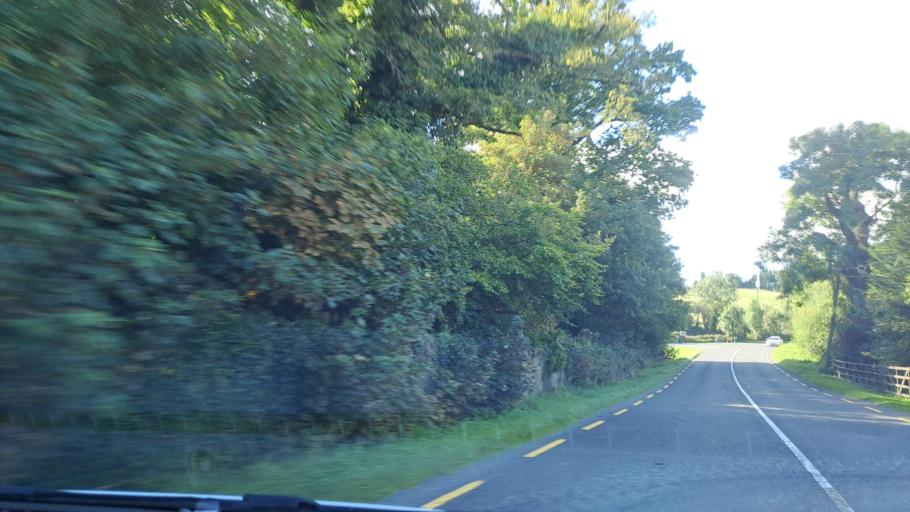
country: IE
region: Ulster
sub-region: County Monaghan
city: Carrickmacross
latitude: 53.9558
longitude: -6.7542
